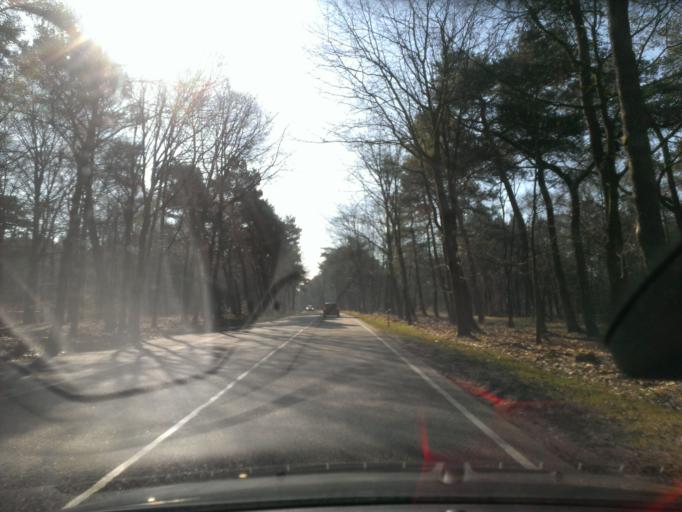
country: NL
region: Gelderland
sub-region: Gemeente Heerde
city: Heerde
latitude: 52.4203
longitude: 6.0128
